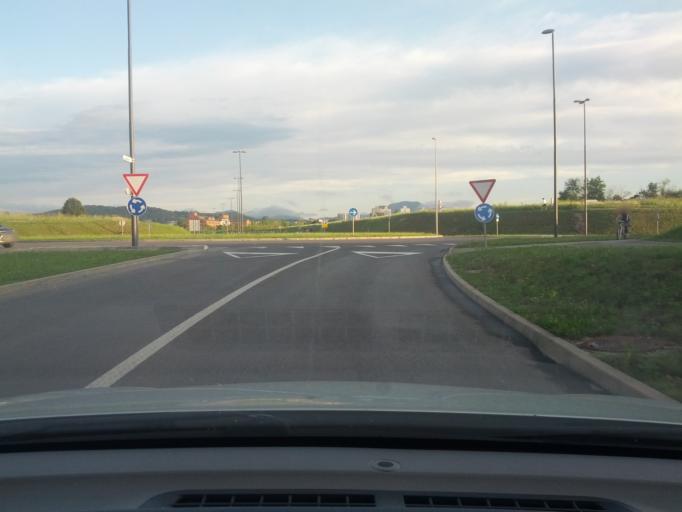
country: SI
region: Ljubljana
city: Ljubljana
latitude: 46.0759
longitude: 14.5247
